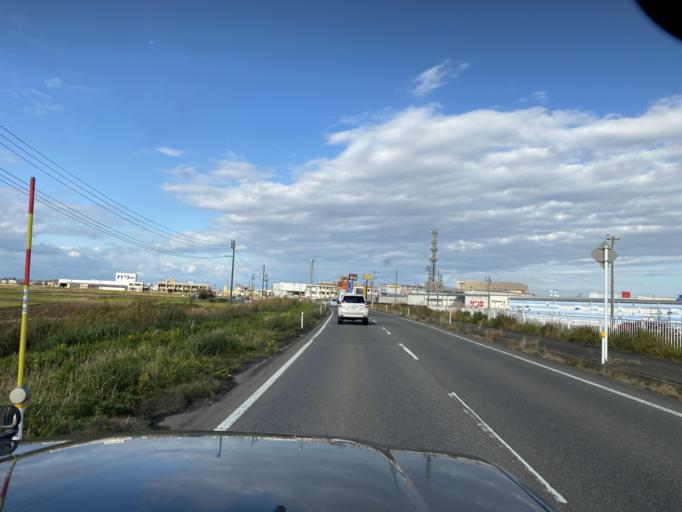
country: JP
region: Niigata
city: Niitsu-honcho
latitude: 37.7838
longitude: 139.1117
